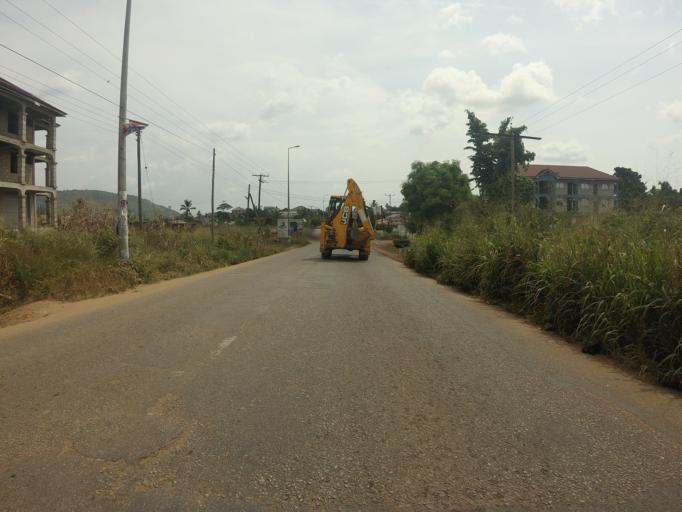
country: GH
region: Eastern
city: Koforidua
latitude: 6.0430
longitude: -0.2609
